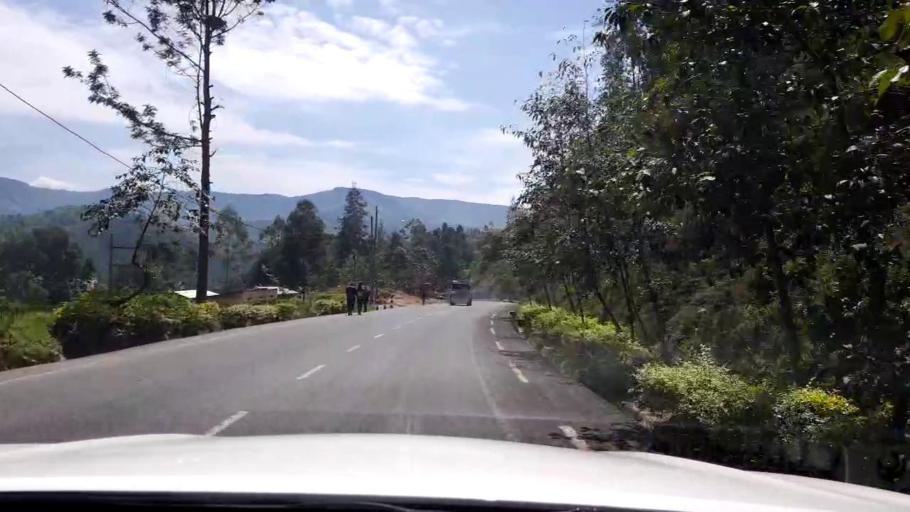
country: RW
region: Southern Province
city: Gitarama
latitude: -1.9218
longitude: 29.6516
